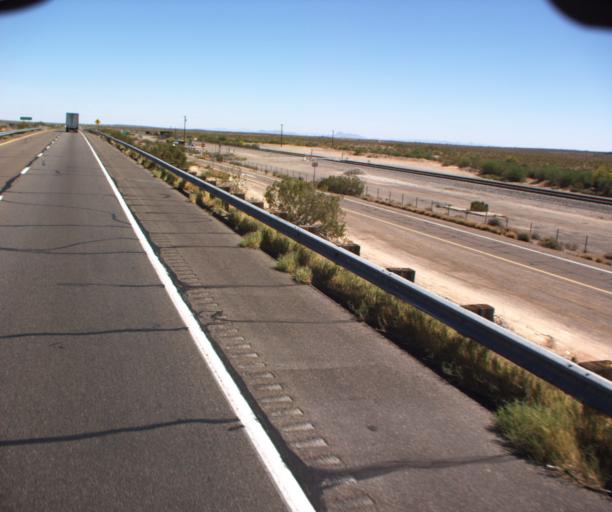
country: US
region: Arizona
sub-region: Maricopa County
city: Gila Bend
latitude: 32.8581
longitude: -113.2148
